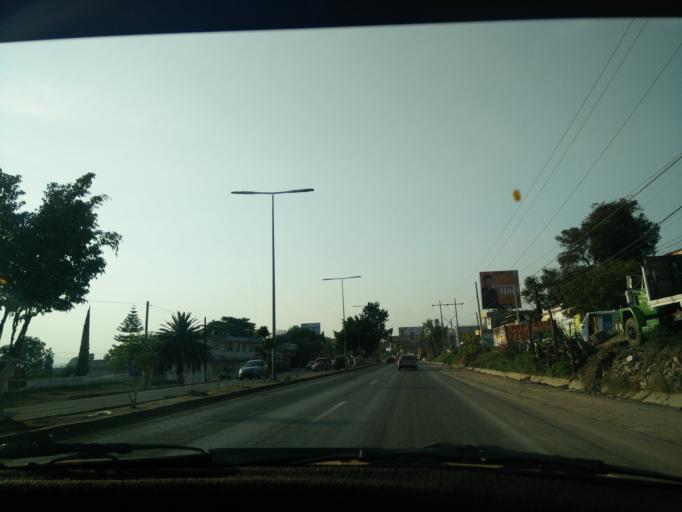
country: MX
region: Oaxaca
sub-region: Santa Maria Atzompa
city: San Jeronimo Yahuiche
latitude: 17.1113
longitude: -96.7559
